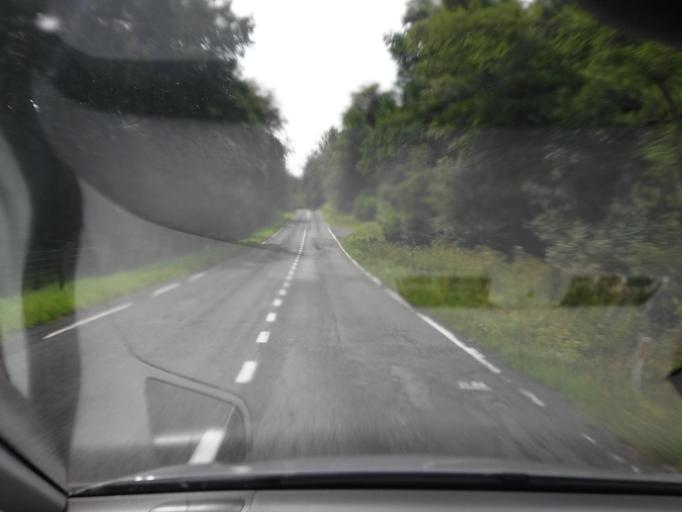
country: BE
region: Wallonia
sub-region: Province du Luxembourg
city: Chiny
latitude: 49.7777
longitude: 5.3491
